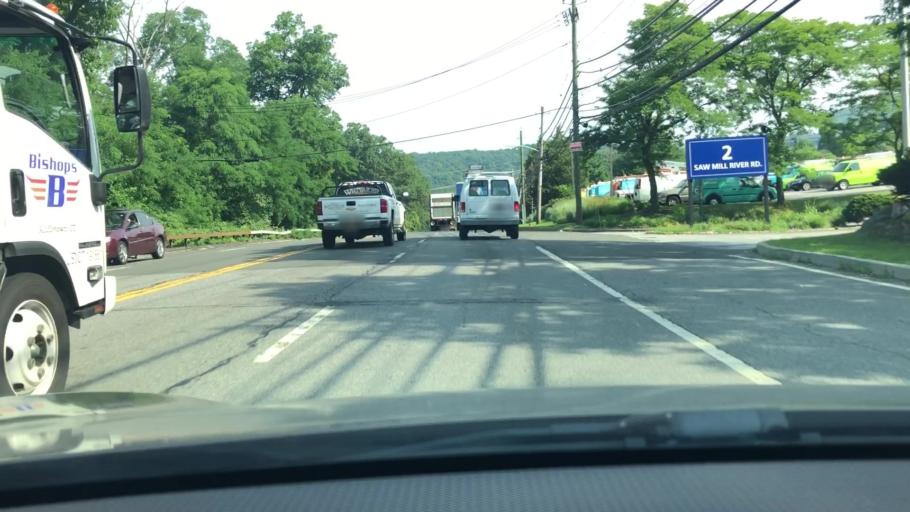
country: US
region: New York
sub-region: Westchester County
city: Elmsford
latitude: 41.0832
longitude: -73.8187
